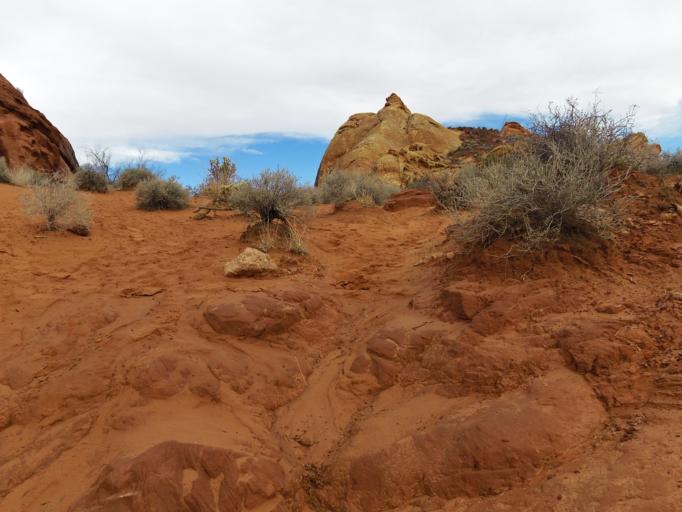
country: US
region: Nevada
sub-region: Clark County
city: Moapa Valley
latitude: 36.4491
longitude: -114.5113
